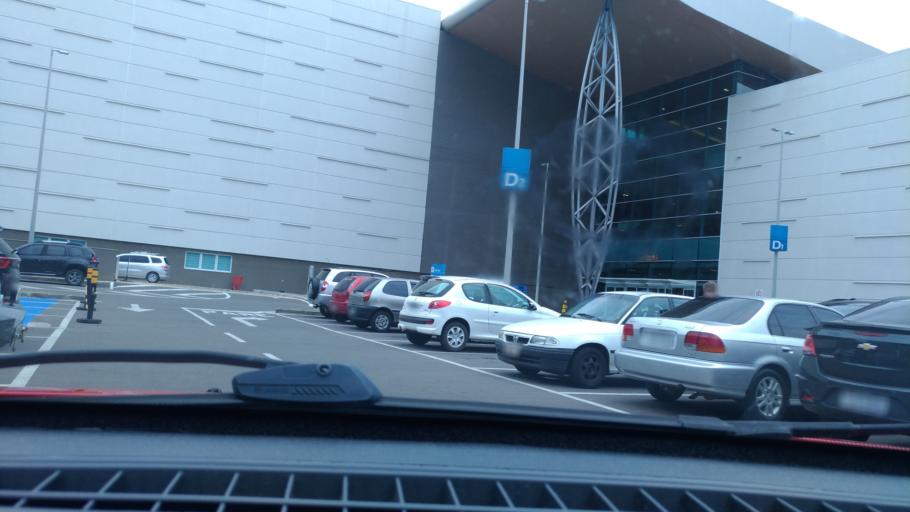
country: BR
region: Rio Grande do Sul
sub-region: Canoas
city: Canoas
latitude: -29.9139
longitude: -51.1640
